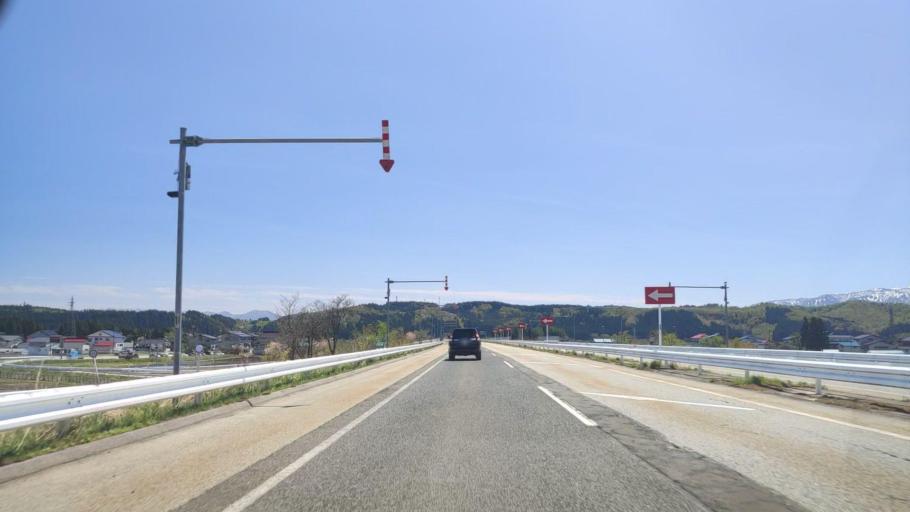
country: JP
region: Yamagata
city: Shinjo
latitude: 38.7045
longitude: 140.3092
